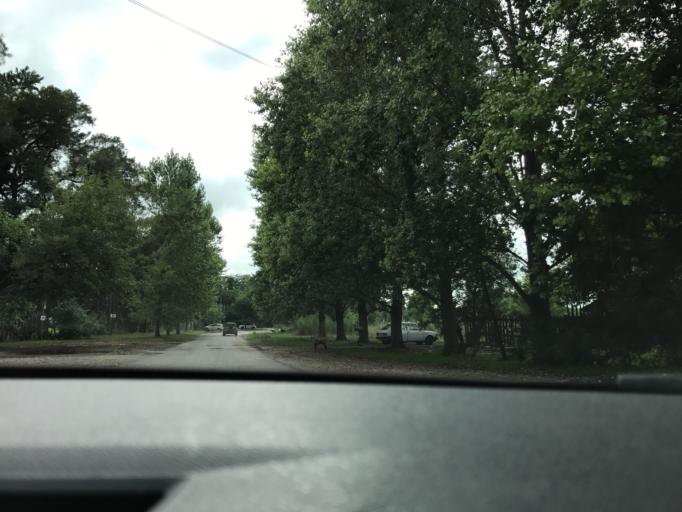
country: AR
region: Buenos Aires
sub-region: Partido de La Plata
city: La Plata
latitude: -34.8635
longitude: -58.0461
